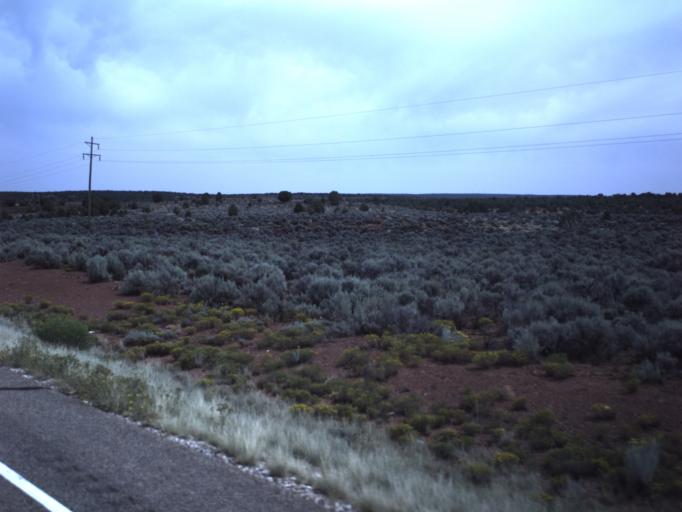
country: US
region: Utah
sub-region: Kane County
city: Kanab
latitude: 37.1258
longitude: -112.0963
